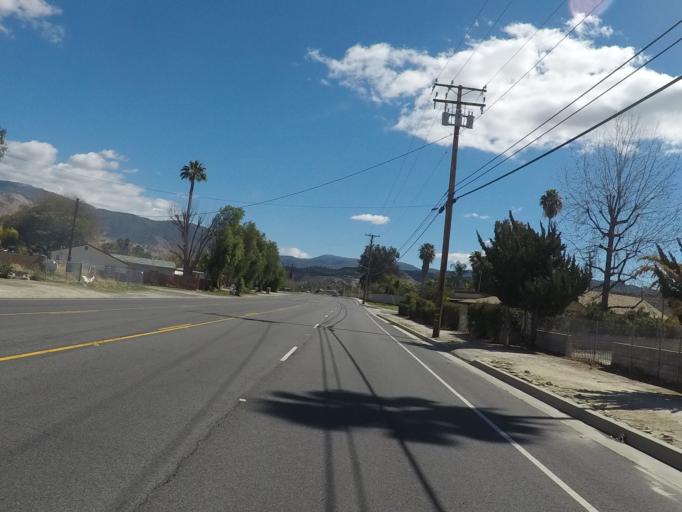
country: US
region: California
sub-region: Riverside County
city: Valle Vista
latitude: 33.7446
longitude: -116.8636
